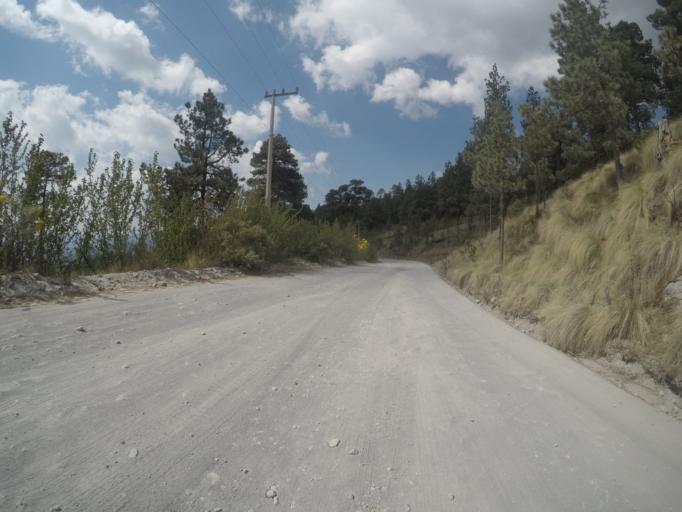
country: MX
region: Mexico
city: Cerro La Calera
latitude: 19.1418
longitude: -99.8016
